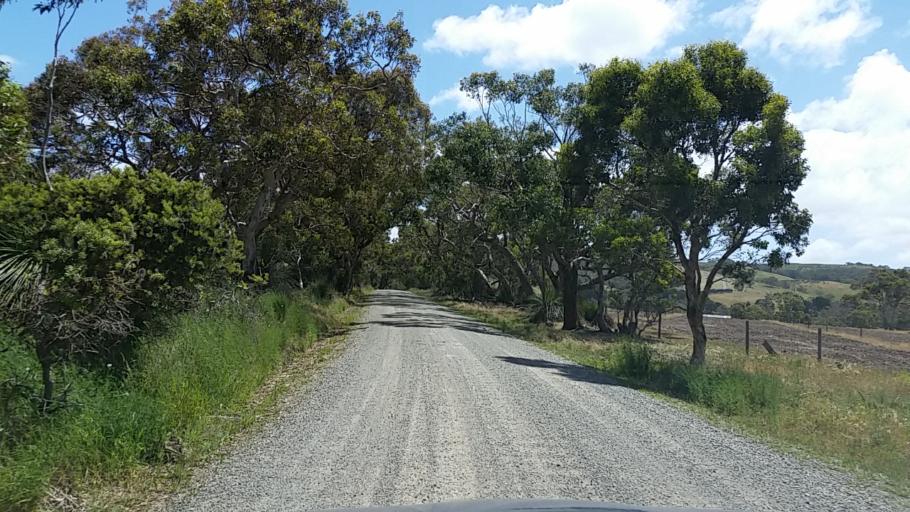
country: AU
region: South Australia
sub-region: Alexandrina
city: Mount Compass
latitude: -35.4363
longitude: 138.5885
